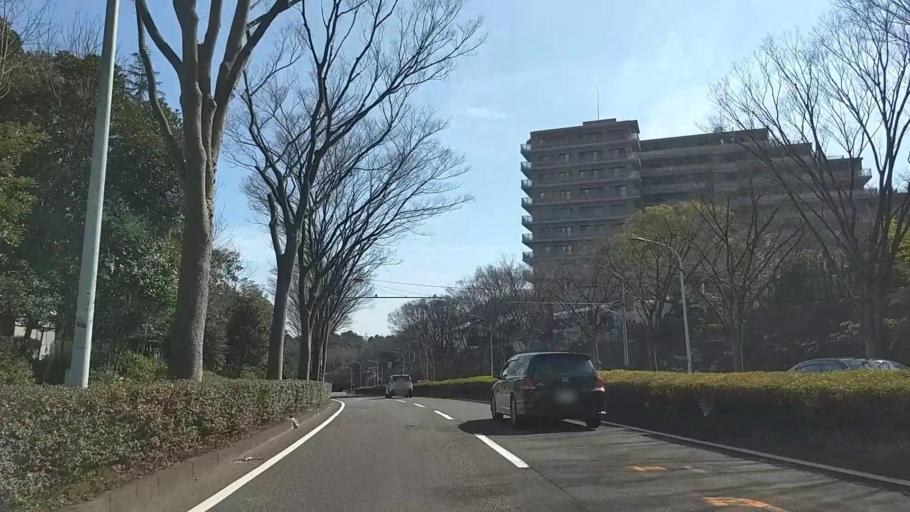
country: JP
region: Kanagawa
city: Fujisawa
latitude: 35.3547
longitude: 139.4430
